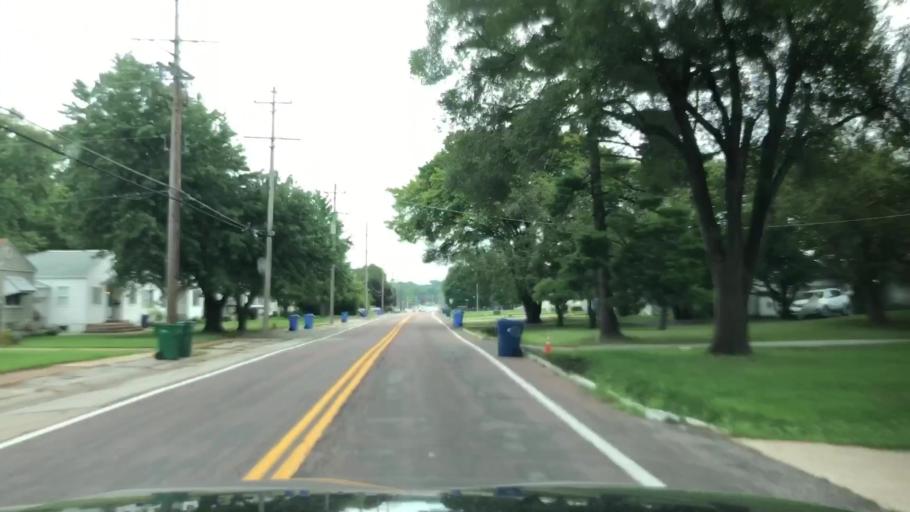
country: US
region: Missouri
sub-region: Saint Louis County
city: Florissant
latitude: 38.7993
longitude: -90.3430
